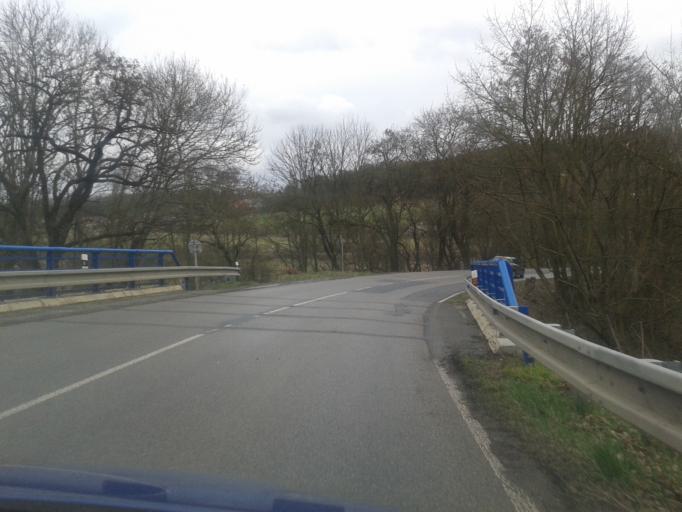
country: CZ
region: Central Bohemia
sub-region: Okres Beroun
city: Lodenice
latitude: 50.0105
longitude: 14.1980
